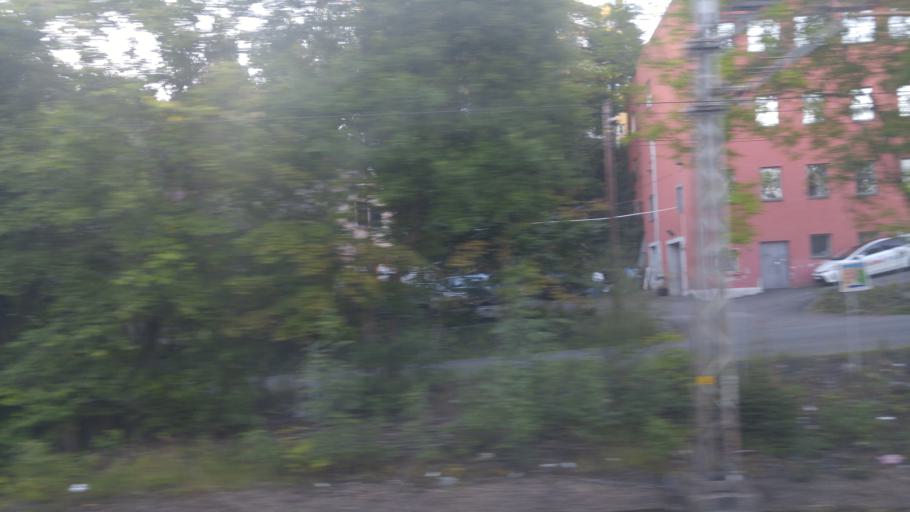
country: NO
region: Oslo
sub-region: Oslo
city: Oslo
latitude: 59.9117
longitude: 10.8260
